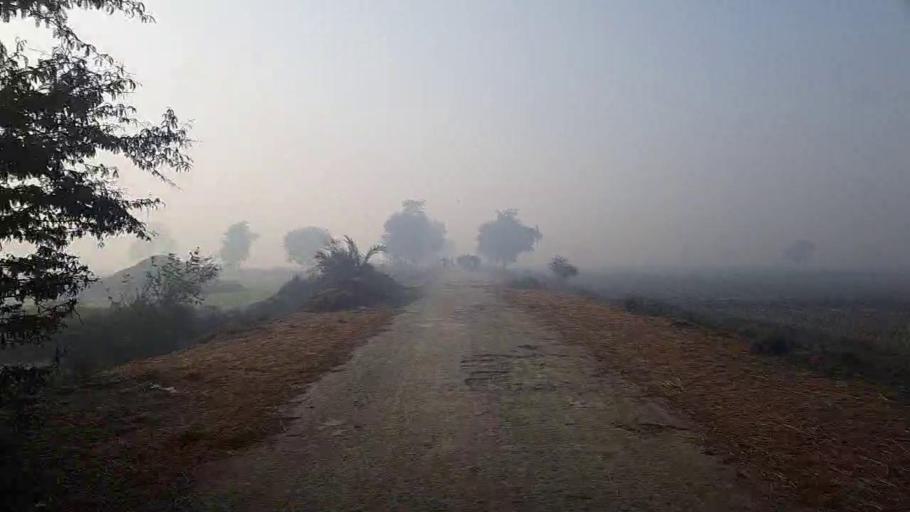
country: PK
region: Sindh
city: Mehar
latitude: 27.1600
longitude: 67.8241
